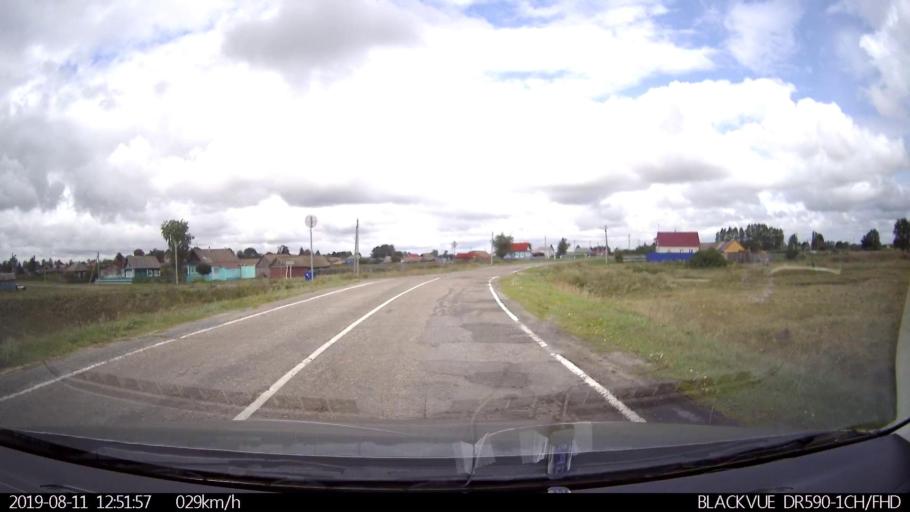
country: RU
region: Ulyanovsk
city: Ignatovka
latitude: 53.8768
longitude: 47.6610
